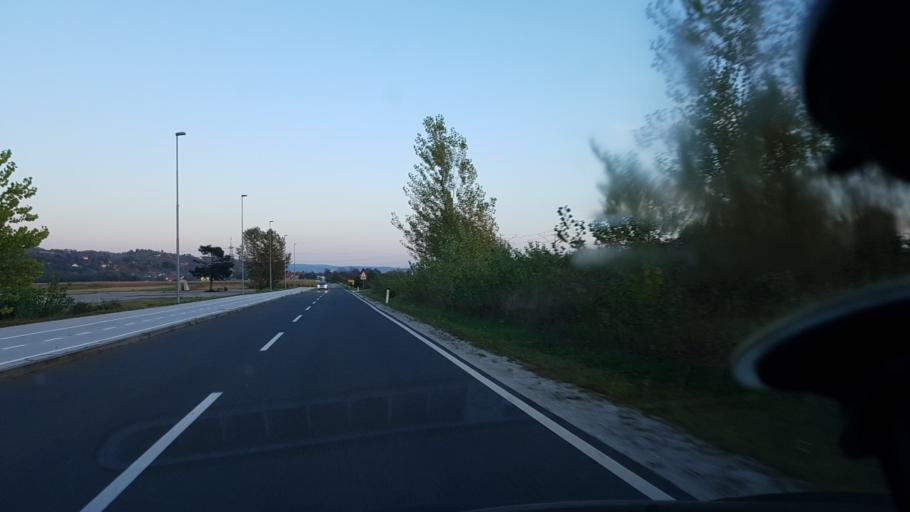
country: HR
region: Zagrebacka
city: Bregana
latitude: 45.8954
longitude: 15.6662
